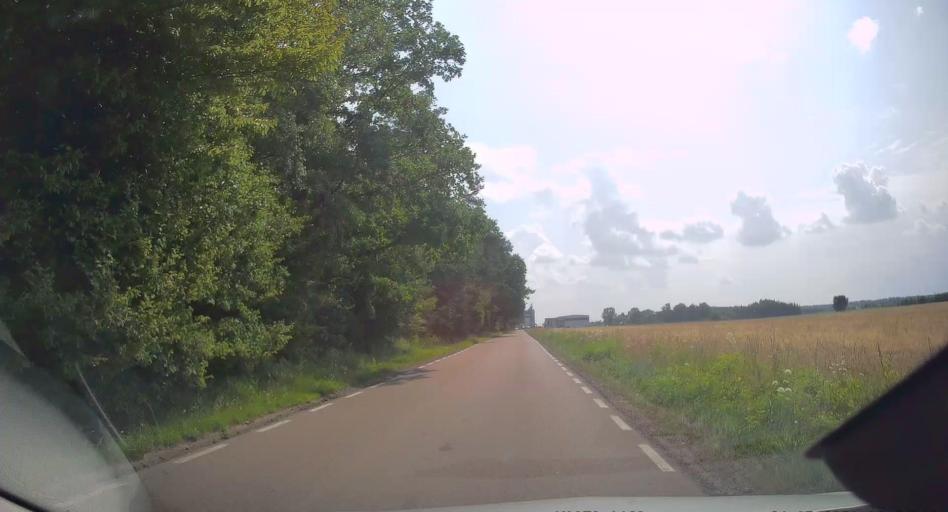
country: PL
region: Lodz Voivodeship
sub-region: Powiat tomaszowski
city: Lubochnia
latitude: 51.5752
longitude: 20.0760
